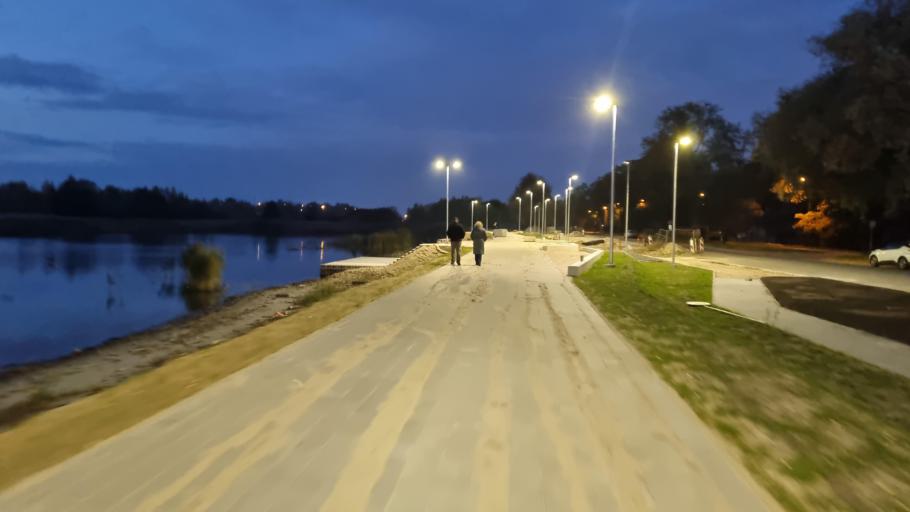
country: LV
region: Riga
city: Daugavgriva
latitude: 57.0326
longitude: 24.0350
